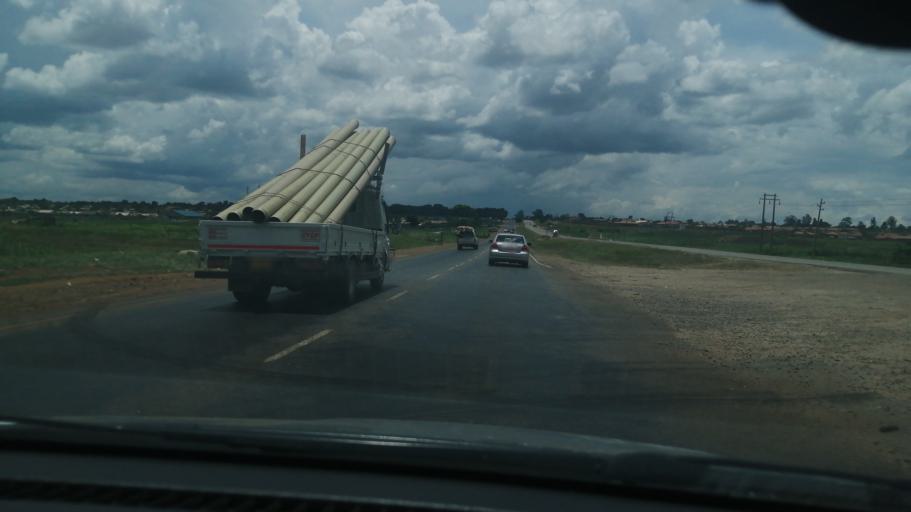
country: ZW
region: Harare
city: Harare
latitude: -17.8196
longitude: 30.9095
